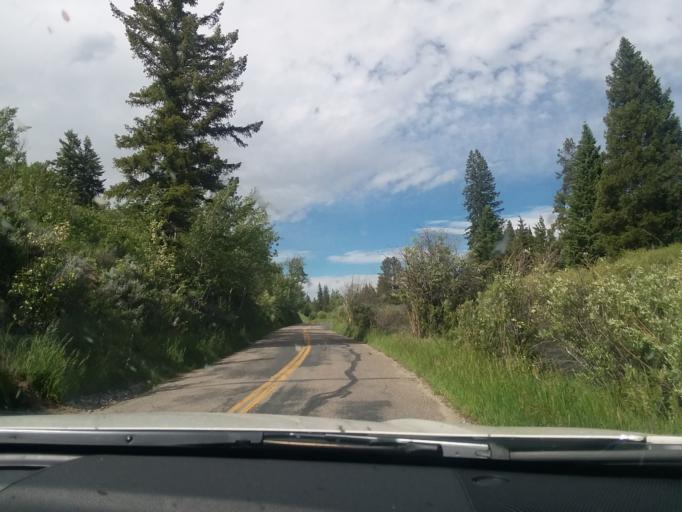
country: US
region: Wyoming
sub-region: Teton County
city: Moose Wilson Road
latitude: 43.5226
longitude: -110.8641
